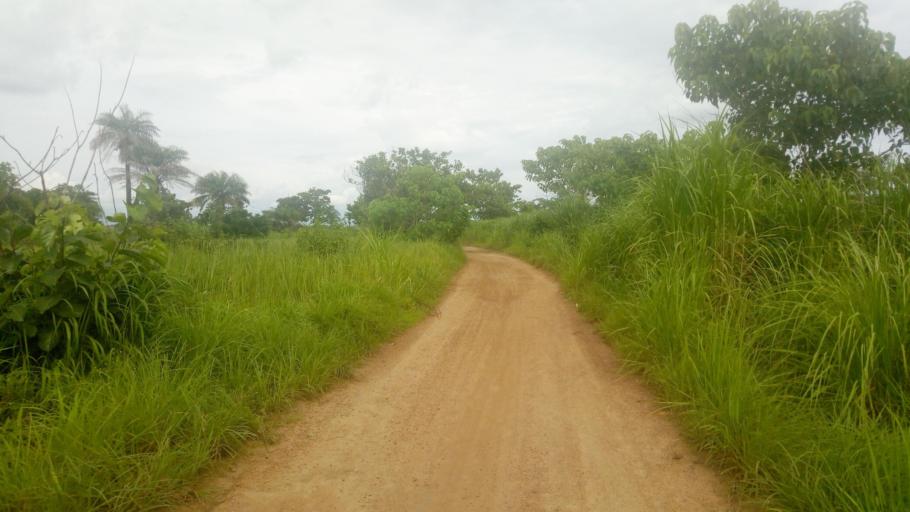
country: SL
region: Northern Province
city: Magburaka
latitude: 8.6716
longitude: -12.0305
